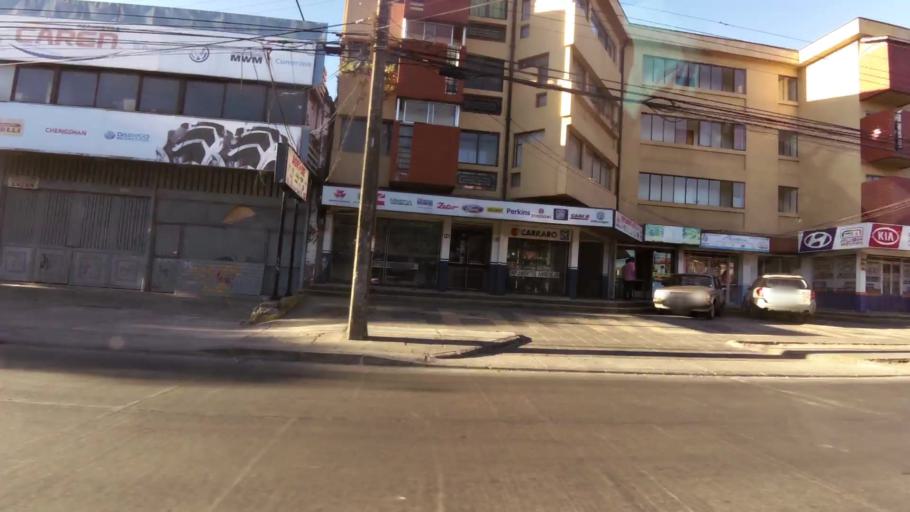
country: CL
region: Maule
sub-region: Provincia de Curico
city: Curico
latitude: -34.9809
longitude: -71.2370
